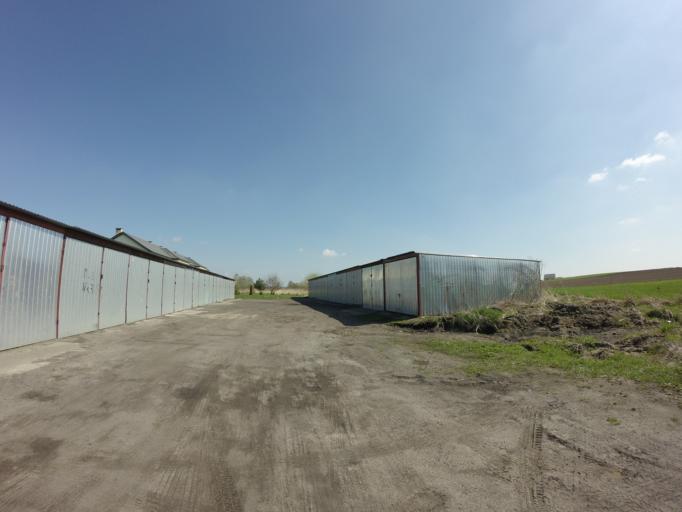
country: PL
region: West Pomeranian Voivodeship
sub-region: Powiat choszczenski
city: Choszczno
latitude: 53.1601
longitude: 15.4371
